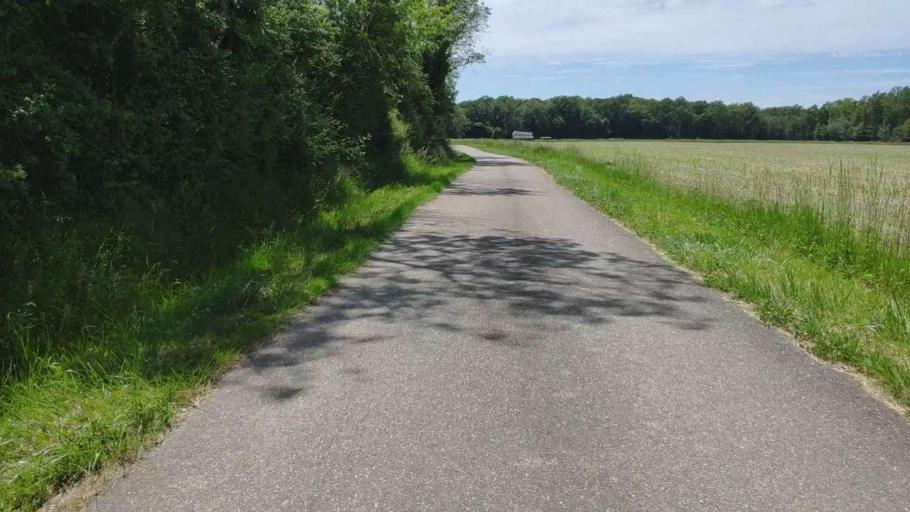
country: FR
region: Franche-Comte
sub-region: Departement du Jura
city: Bletterans
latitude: 46.7804
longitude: 5.3778
